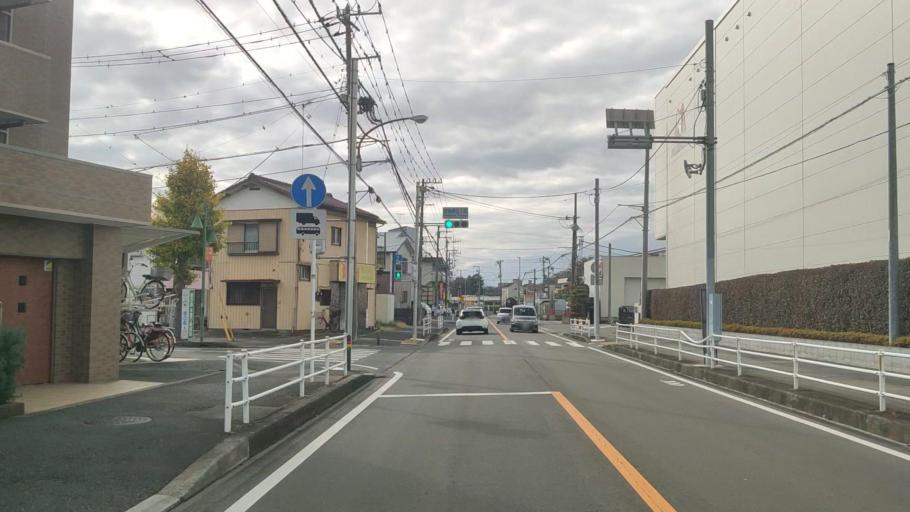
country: JP
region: Kanagawa
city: Minami-rinkan
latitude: 35.4850
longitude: 139.4436
